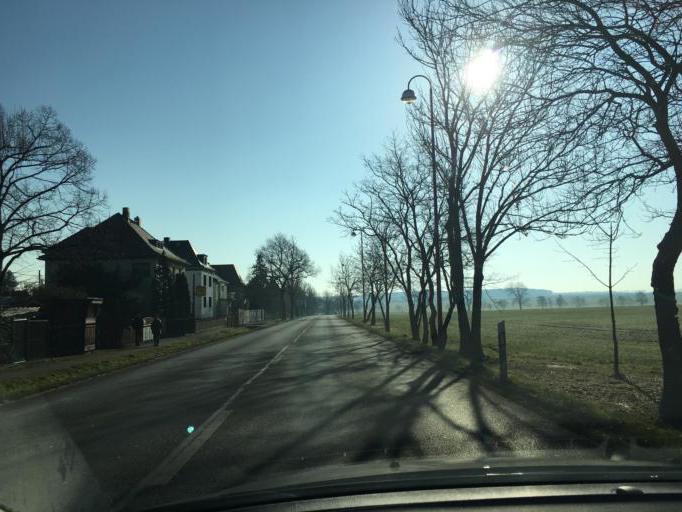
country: DE
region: Saxony
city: Grossposna
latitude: 51.2757
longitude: 12.4728
